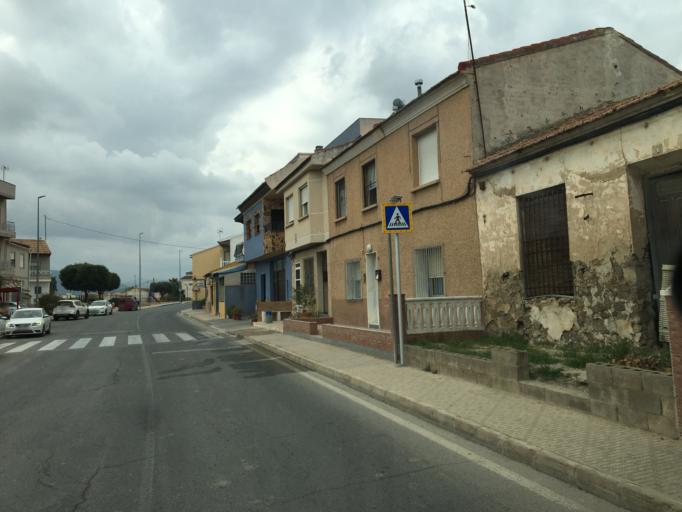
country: ES
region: Murcia
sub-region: Murcia
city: Beniel
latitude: 38.0392
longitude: -1.0103
